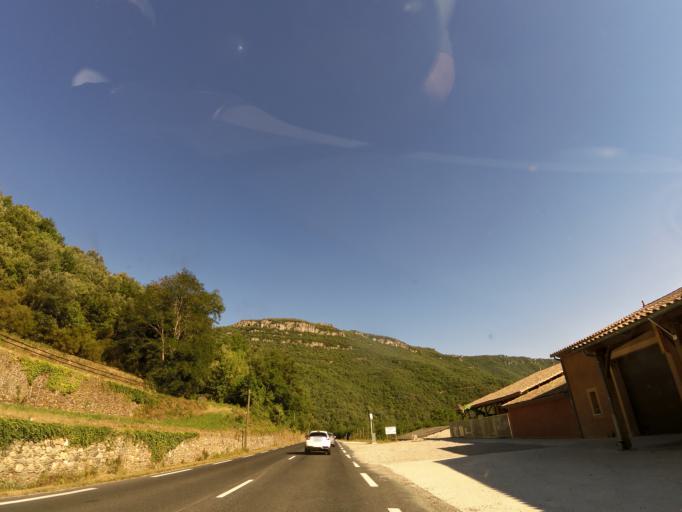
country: FR
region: Languedoc-Roussillon
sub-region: Departement du Gard
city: Sumene
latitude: 43.9724
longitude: 3.6887
